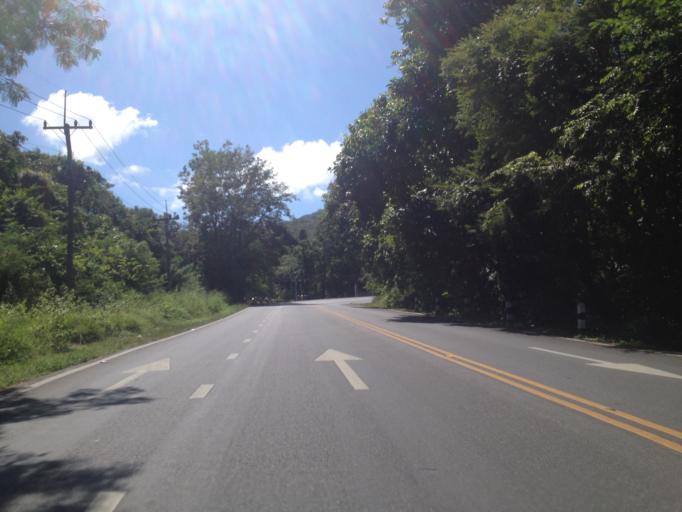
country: TH
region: Chiang Mai
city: Chiang Mai
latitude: 18.8130
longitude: 98.9425
